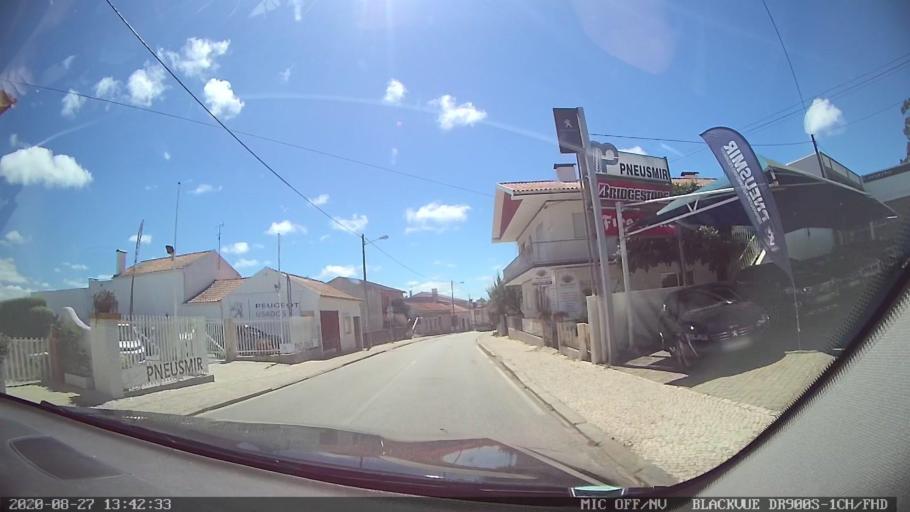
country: PT
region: Coimbra
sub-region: Mira
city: Mira
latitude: 40.4269
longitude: -8.7362
